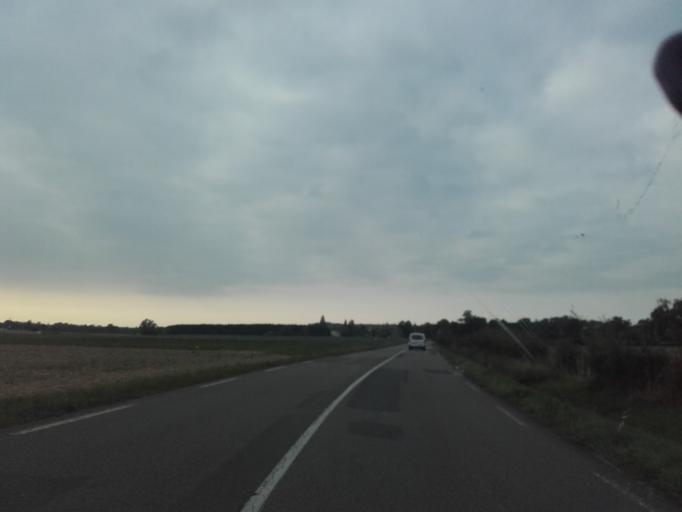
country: FR
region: Bourgogne
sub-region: Departement de Saone-et-Loire
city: Creches-sur-Saone
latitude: 46.2679
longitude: 4.7806
